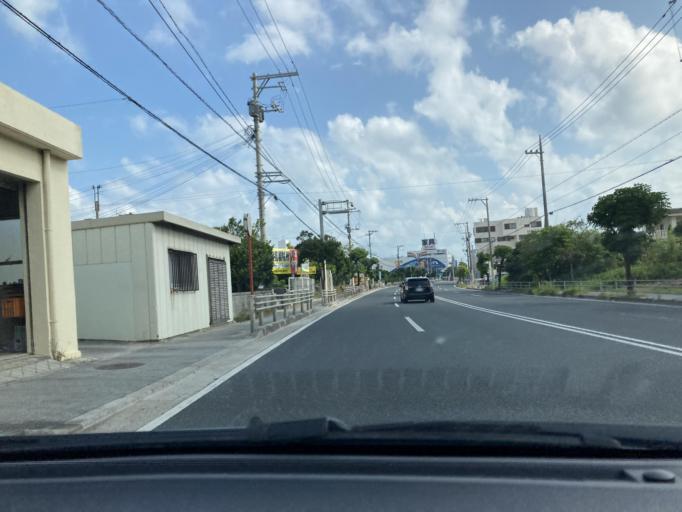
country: JP
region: Okinawa
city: Chatan
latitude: 26.2879
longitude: 127.8143
